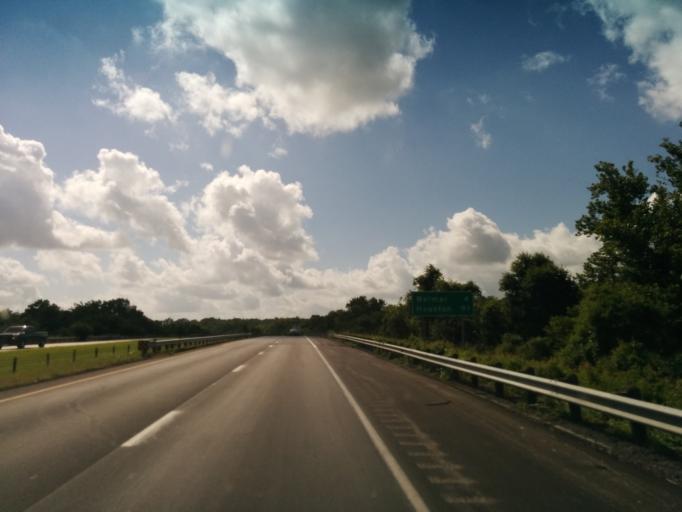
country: US
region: Texas
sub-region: Colorado County
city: Weimar
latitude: 29.6894
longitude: -96.8369
